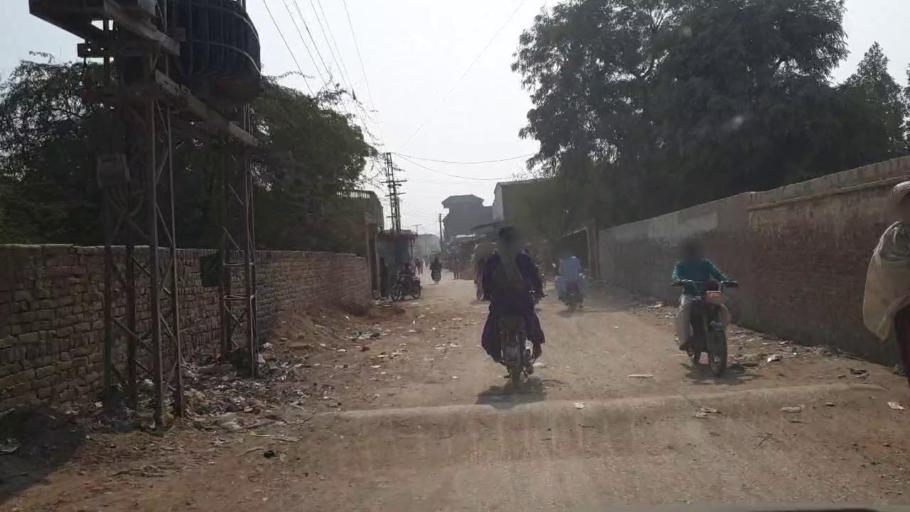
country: PK
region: Sindh
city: Bhit Shah
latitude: 25.8083
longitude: 68.4881
